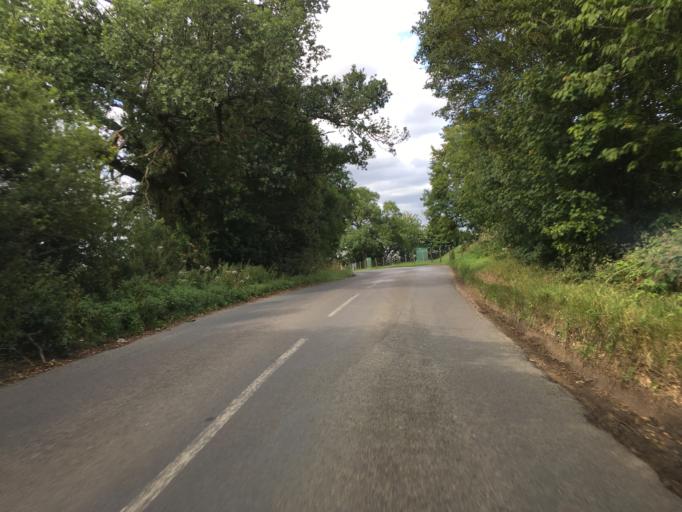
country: GB
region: England
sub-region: Hampshire
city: Overton
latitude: 51.2272
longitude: -1.2613
